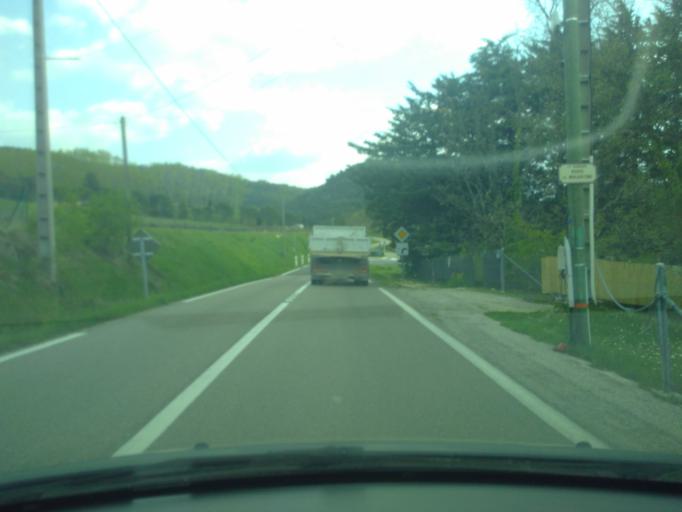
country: FR
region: Provence-Alpes-Cote d'Azur
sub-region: Departement du Vaucluse
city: Malaucene
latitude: 44.1557
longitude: 5.1292
